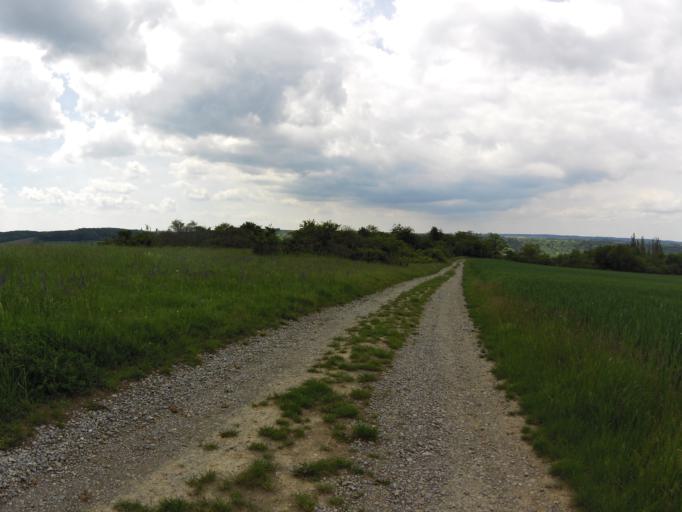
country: DE
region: Bavaria
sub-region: Regierungsbezirk Unterfranken
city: Sommerhausen
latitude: 49.7160
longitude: 10.0254
